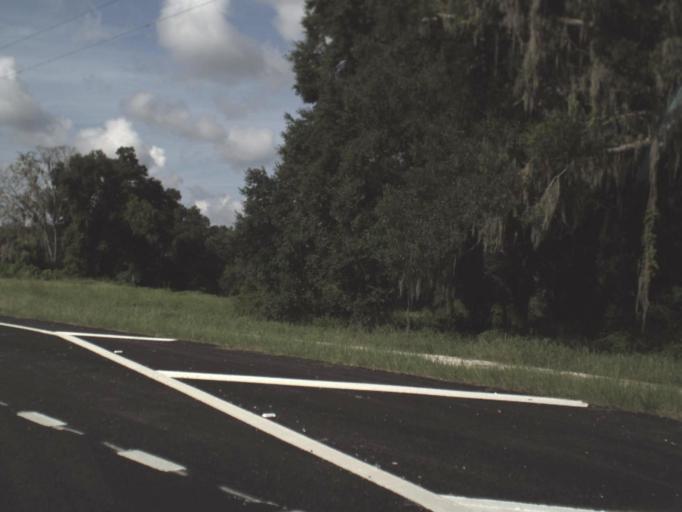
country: US
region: Florida
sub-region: Pasco County
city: Lacoochee
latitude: 28.4363
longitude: -82.1913
